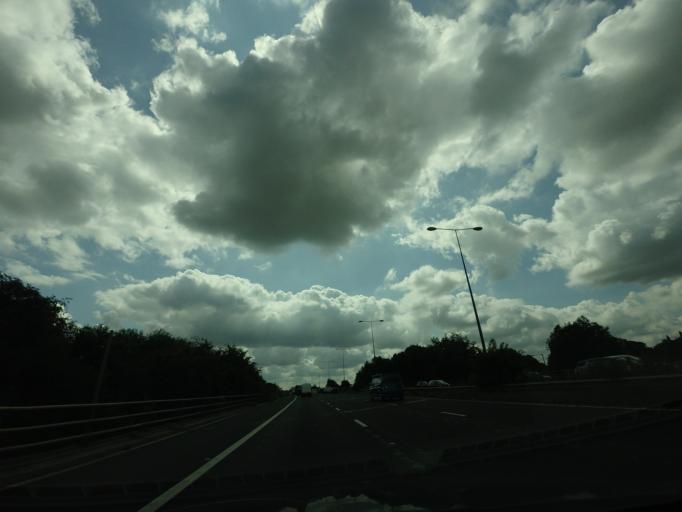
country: GB
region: England
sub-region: Borough of Wigan
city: Shevington
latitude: 53.5523
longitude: -2.7015
